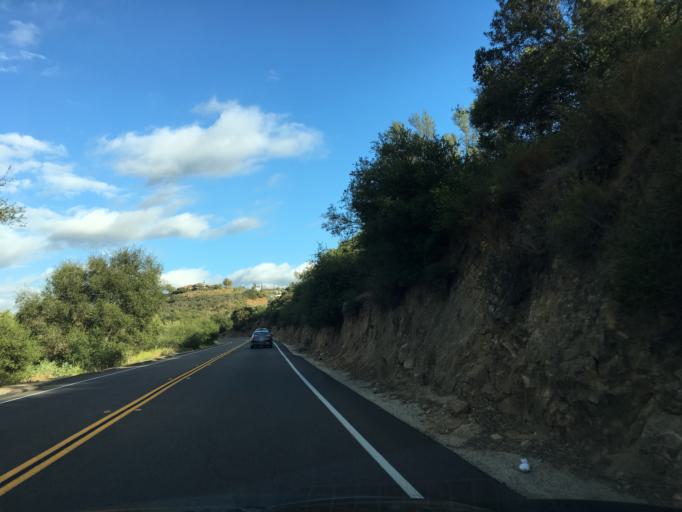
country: US
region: California
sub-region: San Diego County
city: Valley Center
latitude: 33.2545
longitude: -117.0656
